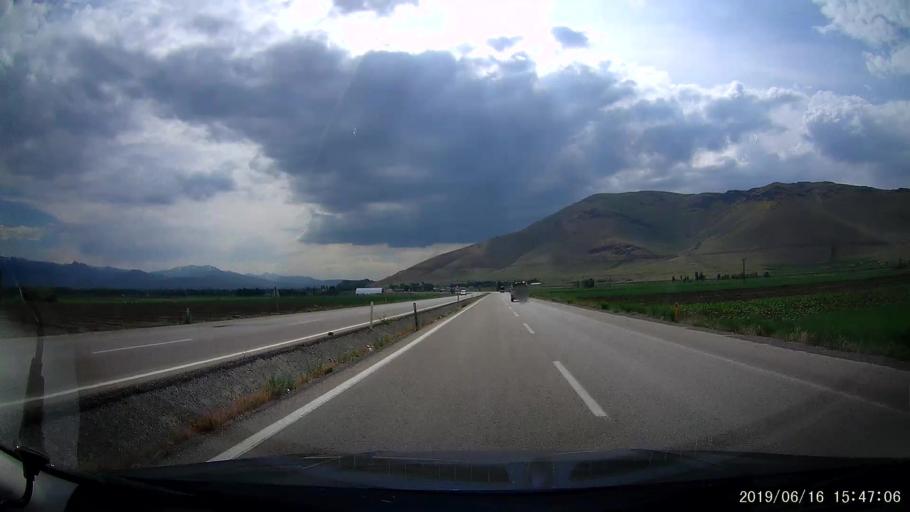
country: TR
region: Erzurum
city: Pasinler
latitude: 39.9889
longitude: 41.7285
